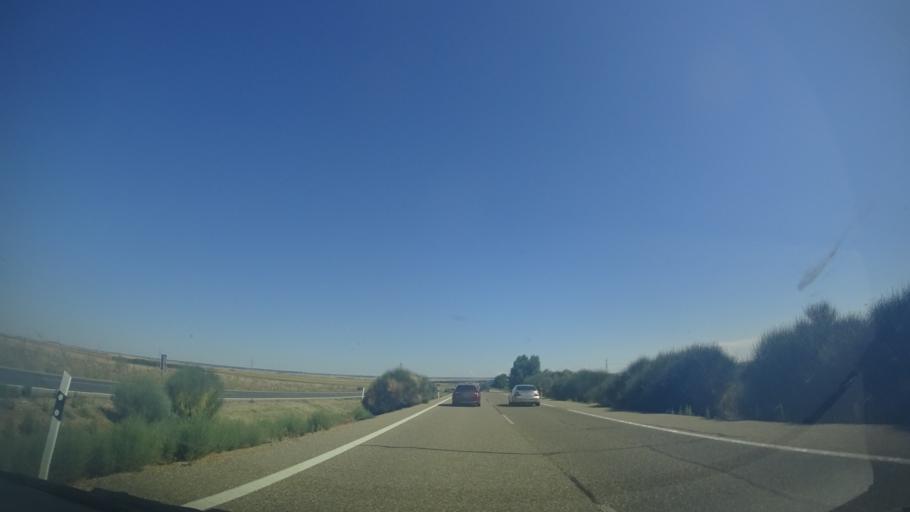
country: ES
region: Castille and Leon
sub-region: Provincia de Zamora
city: Quintanilla del Monte
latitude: 41.8109
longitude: -5.3578
